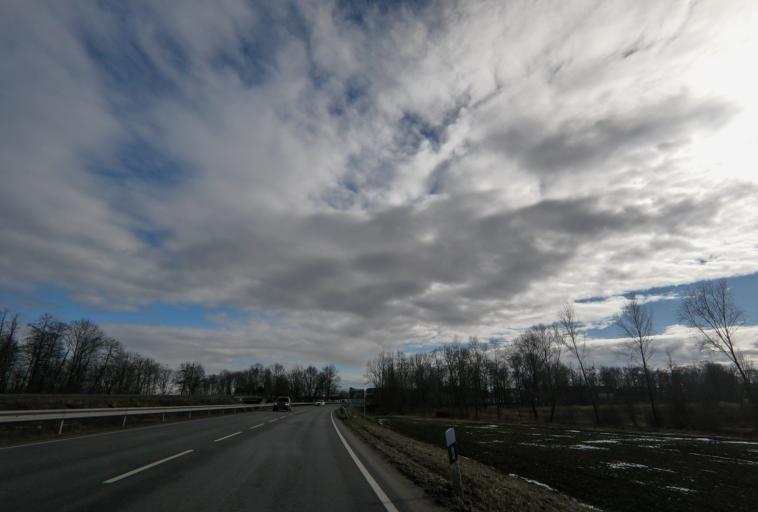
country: DE
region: Bavaria
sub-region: Upper Palatinate
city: Kofering
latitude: 48.9419
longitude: 12.1989
